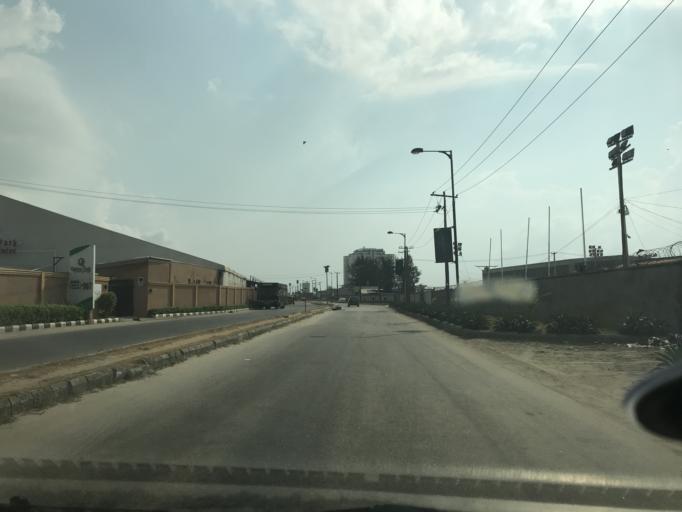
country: NG
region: Lagos
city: Ikoyi
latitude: 6.4241
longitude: 3.4430
